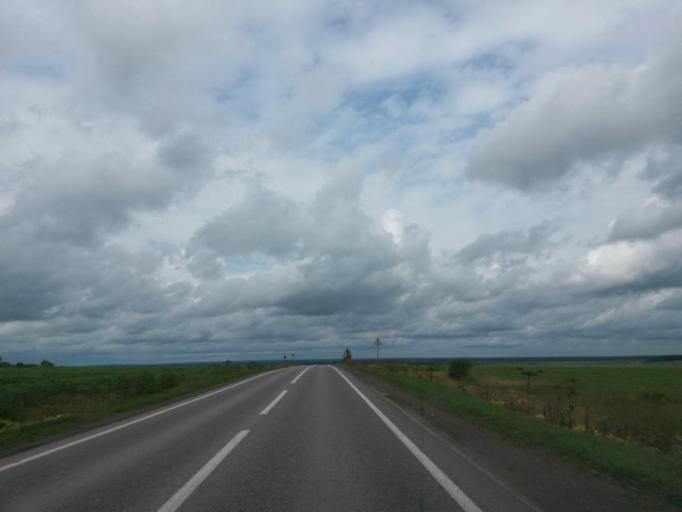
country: RU
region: Jaroslavl
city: Yaroslavl
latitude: 57.7576
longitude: 39.8694
